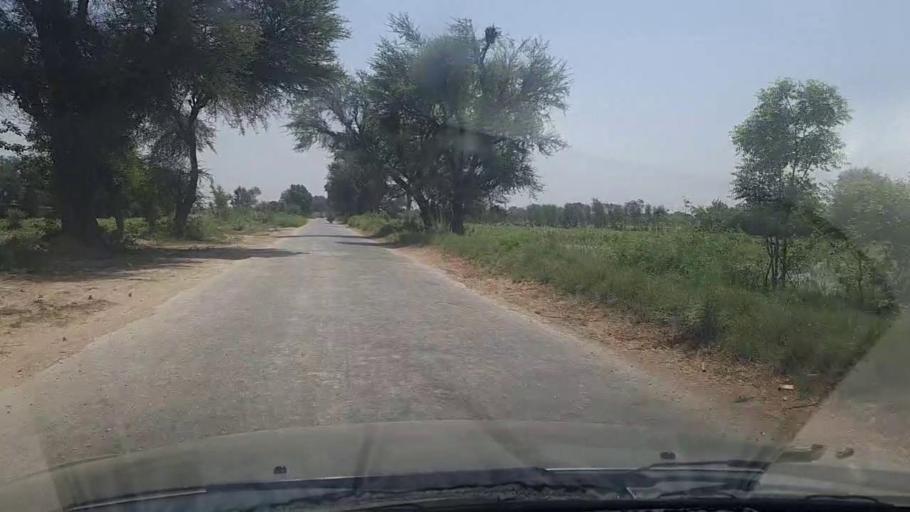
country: PK
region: Sindh
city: Tando Jam
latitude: 25.2819
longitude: 68.6052
